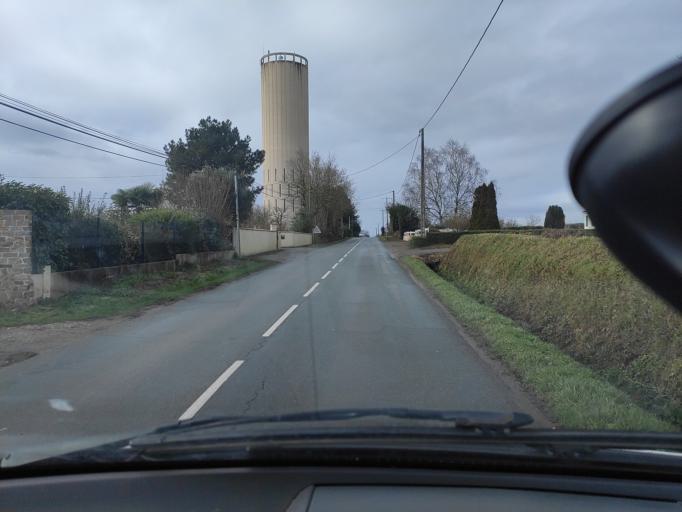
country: FR
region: Pays de la Loire
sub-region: Departement de la Vendee
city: La Boissiere-des-Landes
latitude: 46.5656
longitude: -1.4679
